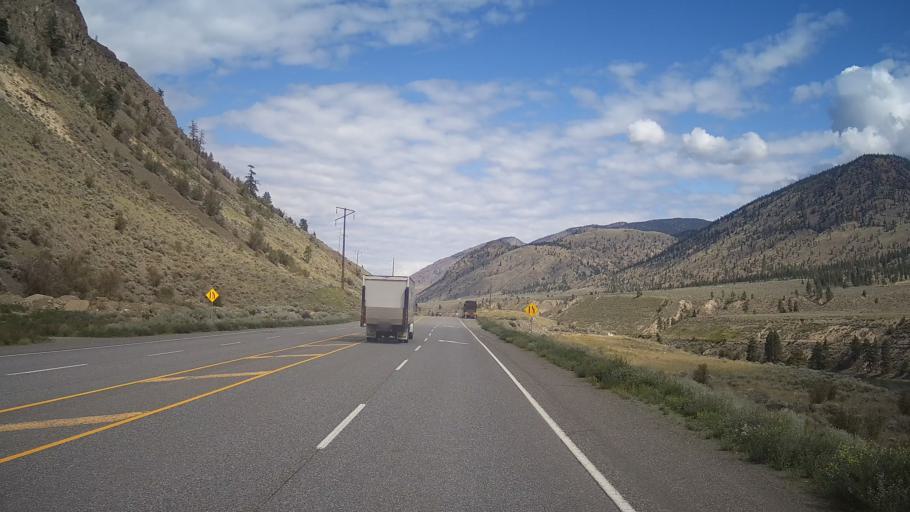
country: CA
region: British Columbia
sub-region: Thompson-Nicola Regional District
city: Ashcroft
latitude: 50.5268
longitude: -121.2856
